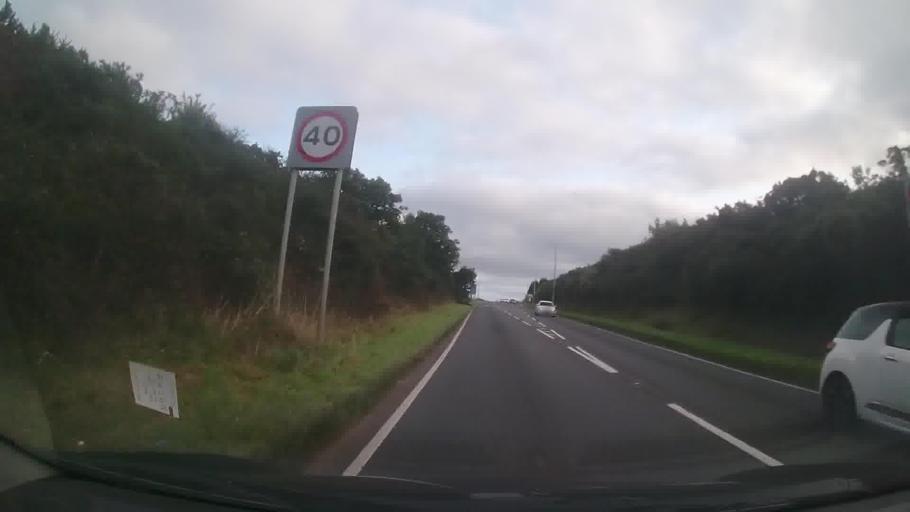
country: GB
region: Wales
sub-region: Pembrokeshire
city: Burton
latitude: 51.7125
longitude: -4.9367
